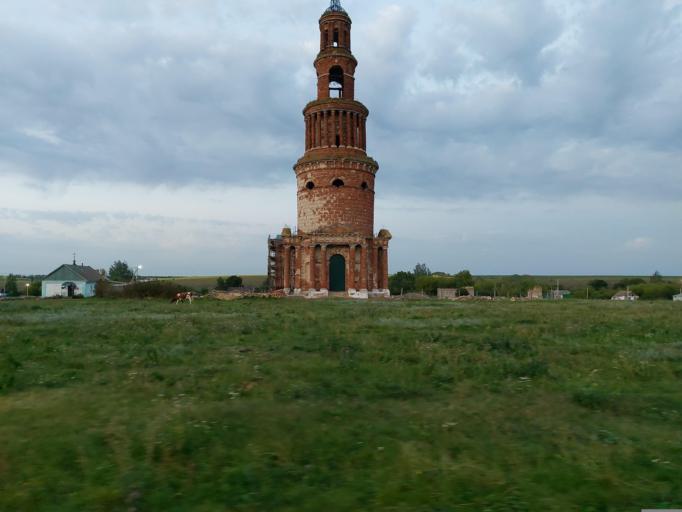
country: RU
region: Lipetsk
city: Dolgorukovo
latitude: 52.3773
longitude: 38.0510
